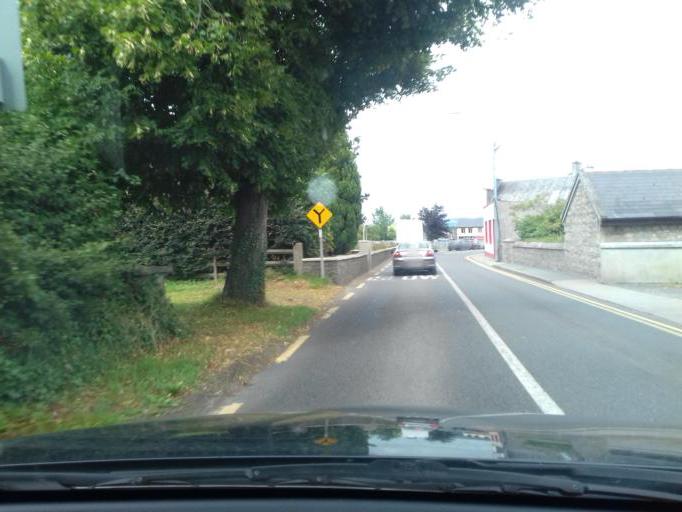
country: IE
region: Leinster
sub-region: Wicklow
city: Baltinglass
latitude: 52.8799
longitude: -6.6961
